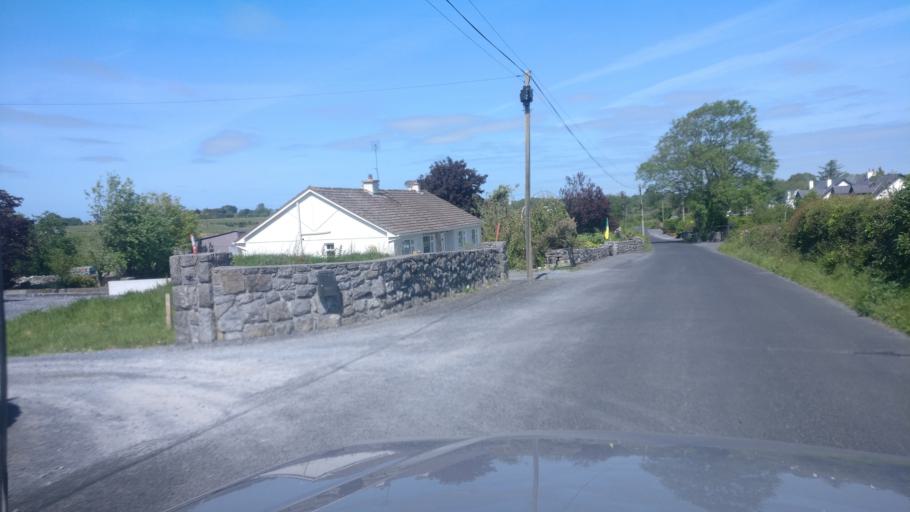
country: IE
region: Connaught
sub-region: County Galway
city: Gort
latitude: 53.0873
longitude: -8.8028
